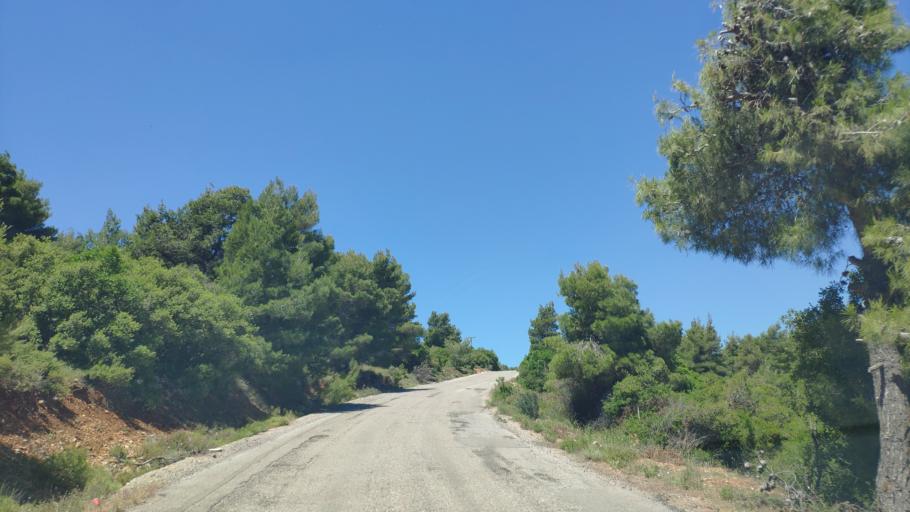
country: GR
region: Central Greece
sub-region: Nomos Voiotias
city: Kaparellion
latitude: 38.2056
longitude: 23.1712
